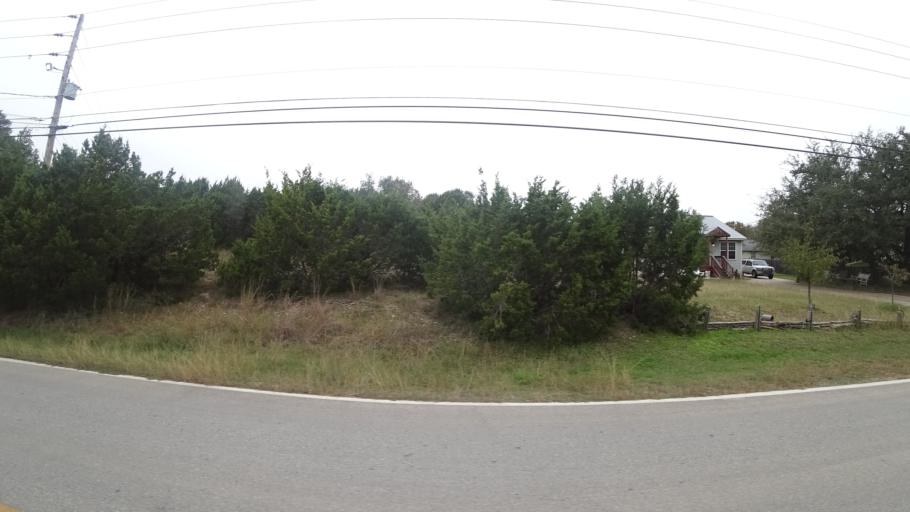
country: US
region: Texas
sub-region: Travis County
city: Lakeway
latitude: 30.3699
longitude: -97.9326
